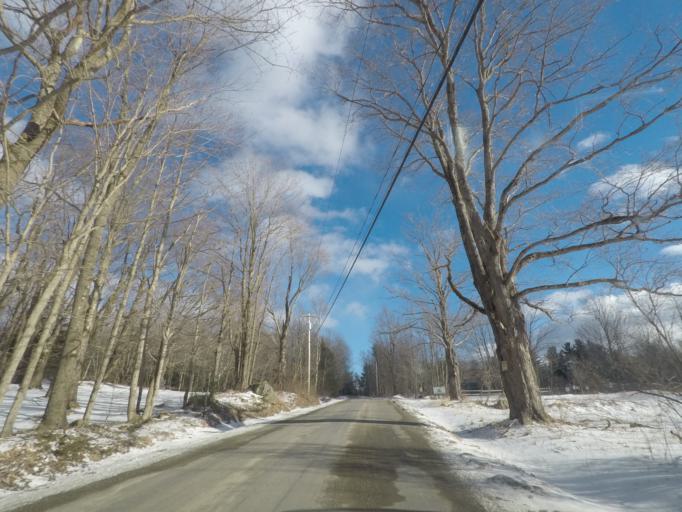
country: US
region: New York
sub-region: Rensselaer County
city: Poestenkill
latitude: 42.7457
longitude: -73.4798
